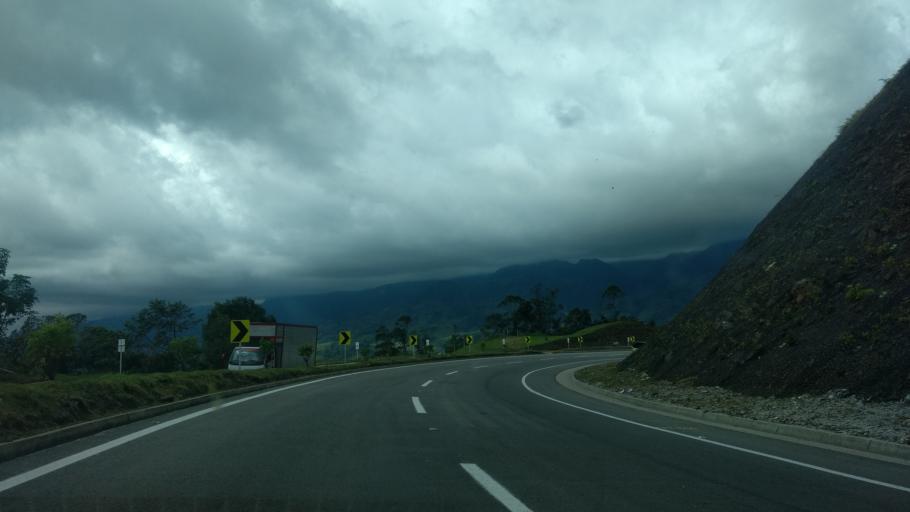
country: CO
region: Cundinamarca
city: San Francisco
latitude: 4.9491
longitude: -74.2985
